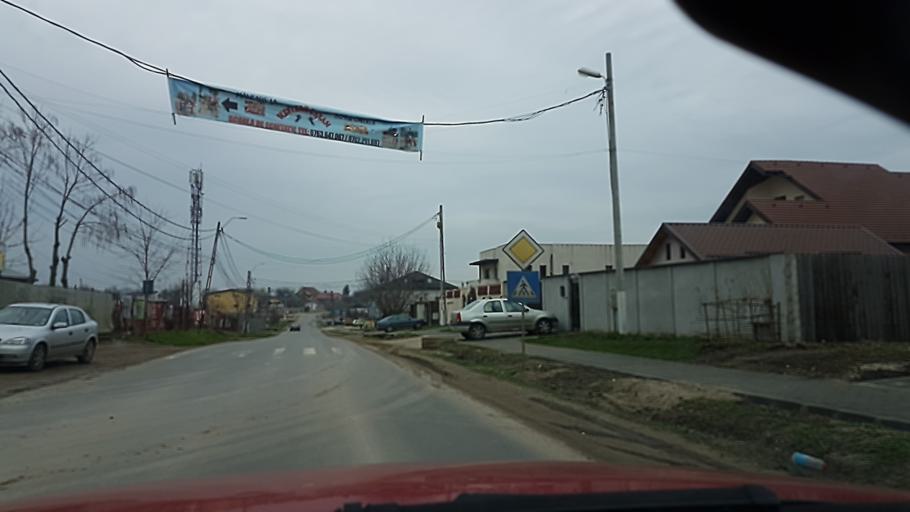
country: RO
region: Ilfov
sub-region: Comuna Tunari
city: Tunari
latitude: 44.5548
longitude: 26.1432
